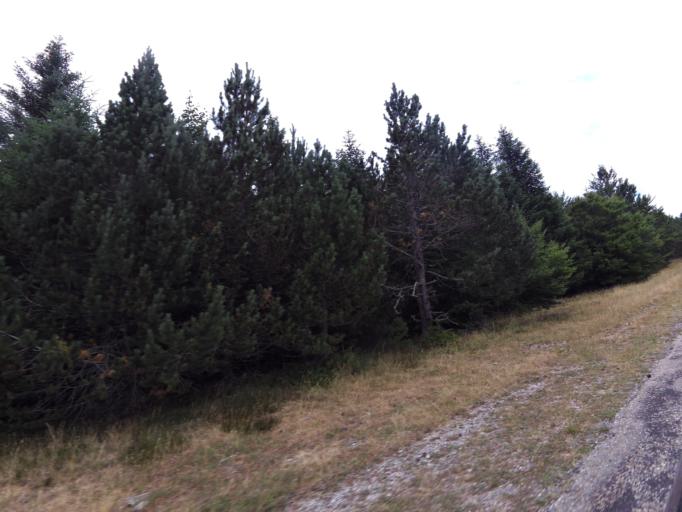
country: FR
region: Languedoc-Roussillon
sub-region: Departement du Gard
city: Valleraugue
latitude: 44.0767
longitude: 3.5795
